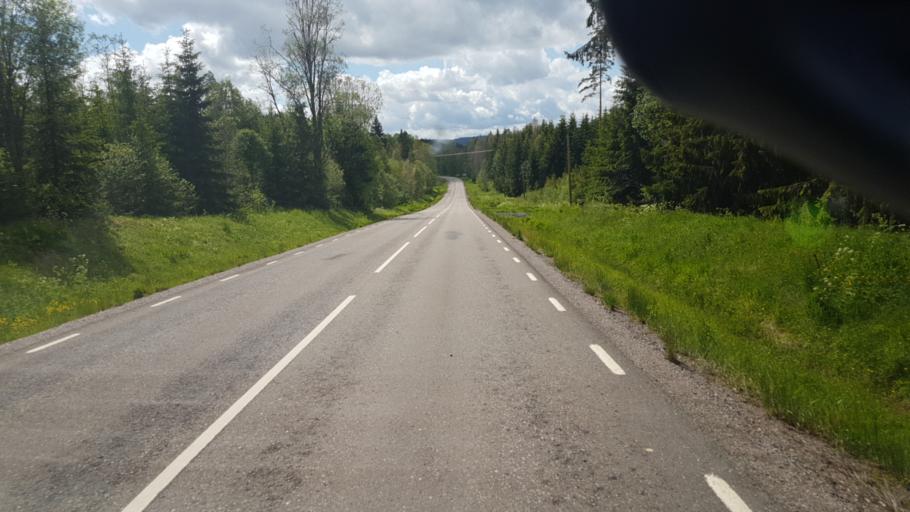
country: SE
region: Vaermland
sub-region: Eda Kommun
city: Amotfors
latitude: 59.7006
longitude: 12.4308
